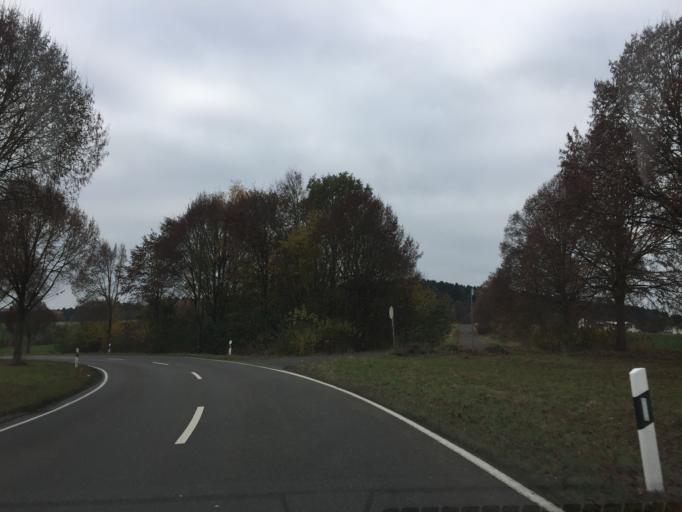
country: DE
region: Rheinland-Pfalz
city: Girod
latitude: 50.4450
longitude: 7.9012
